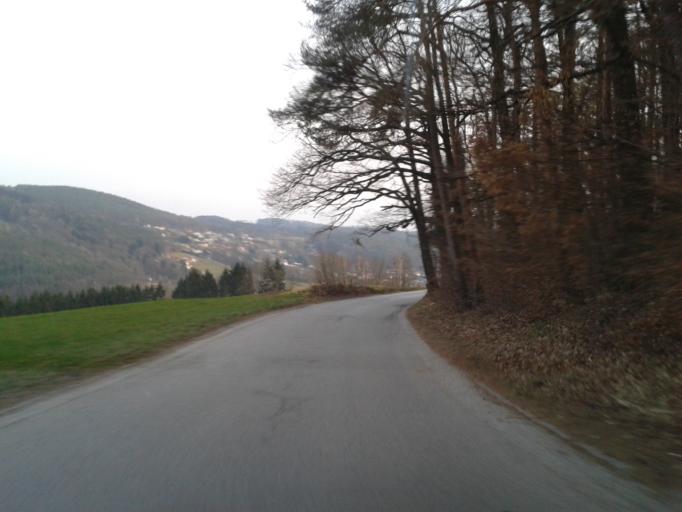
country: AT
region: Styria
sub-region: Politischer Bezirk Graz-Umgebung
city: Stattegg
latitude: 47.1294
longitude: 15.4386
